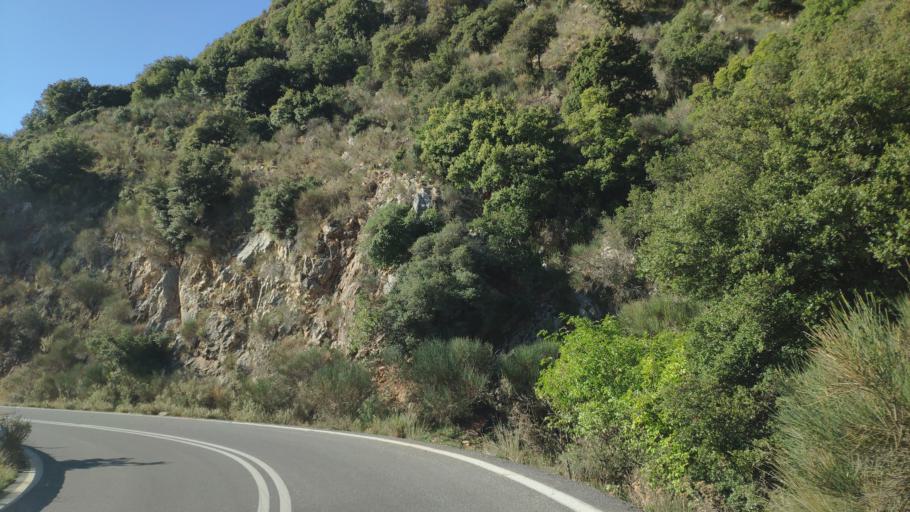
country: GR
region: Peloponnese
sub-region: Nomos Arkadias
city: Dimitsana
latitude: 37.5832
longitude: 22.0546
